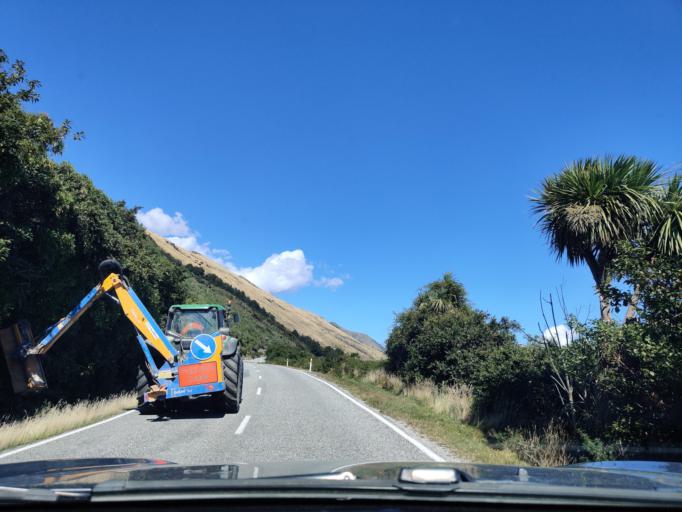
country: NZ
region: Otago
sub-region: Queenstown-Lakes District
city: Queenstown
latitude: -44.9501
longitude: 168.4356
